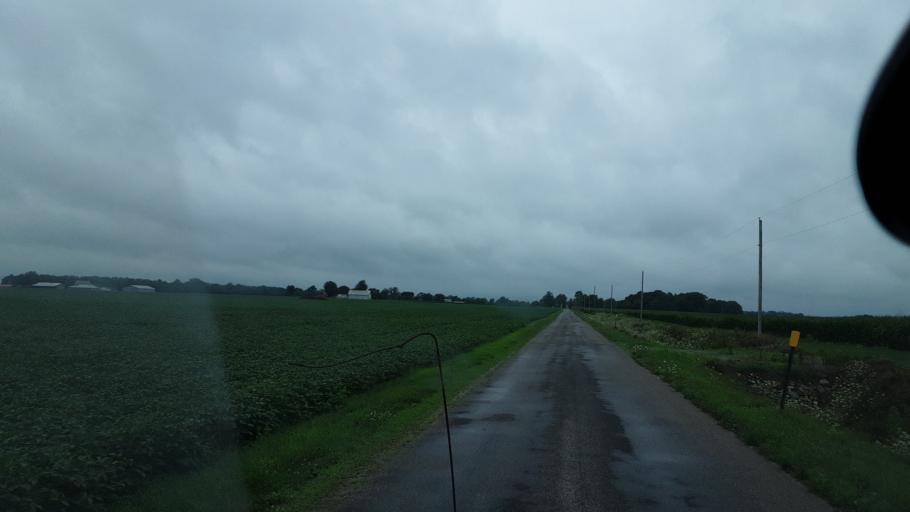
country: US
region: Ohio
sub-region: Van Wert County
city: Convoy
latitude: 40.8297
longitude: -84.7926
